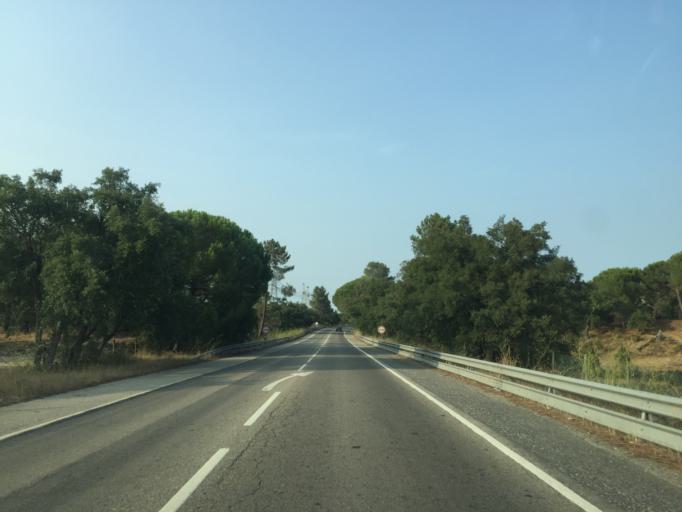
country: PT
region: Setubal
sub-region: Setubal
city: Setubal
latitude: 38.5878
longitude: -8.6777
